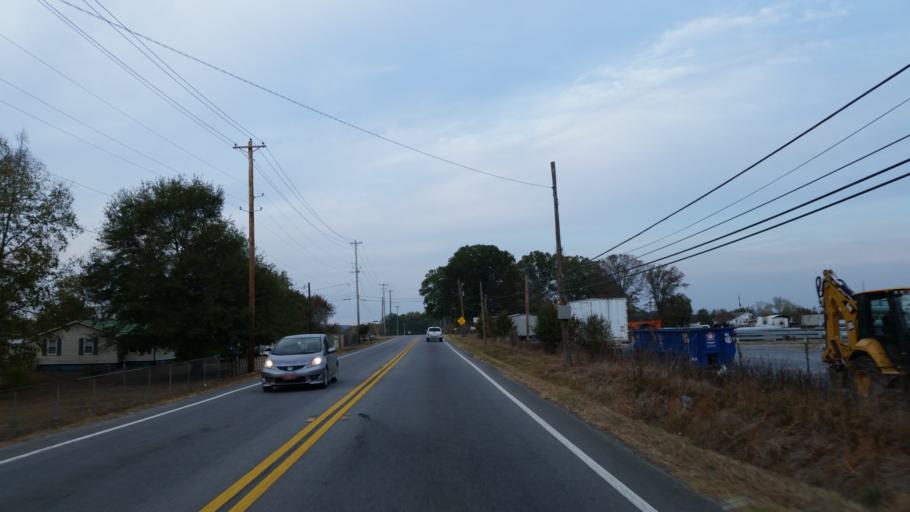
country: US
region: Georgia
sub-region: Gordon County
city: Calhoun
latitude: 34.5687
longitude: -84.9395
